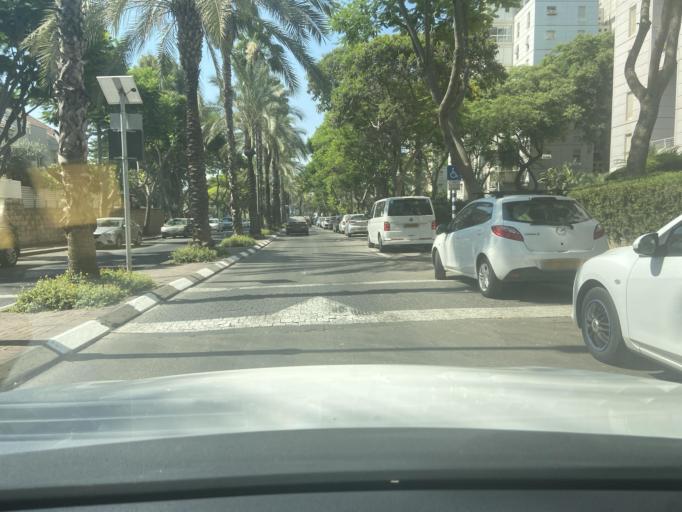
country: IL
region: Central District
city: Yehud
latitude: 32.0317
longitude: 34.8807
